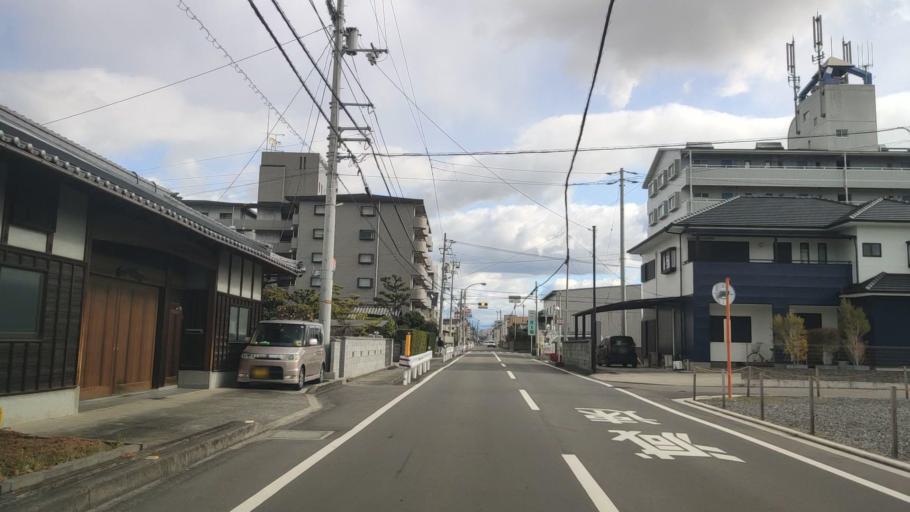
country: JP
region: Ehime
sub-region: Shikoku-chuo Shi
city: Matsuyama
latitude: 33.8096
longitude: 132.7528
